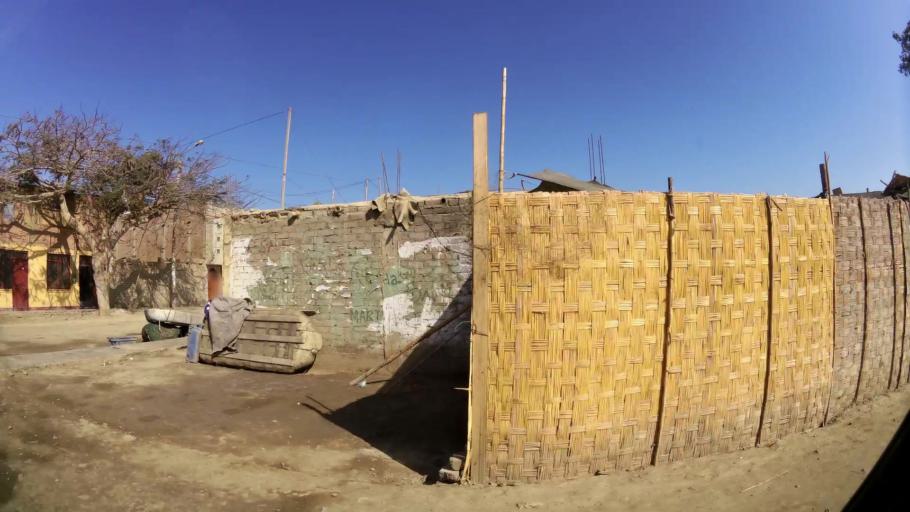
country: PE
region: Ancash
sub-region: Provincia de Huarmey
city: Huarmey
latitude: -10.0626
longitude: -78.1542
